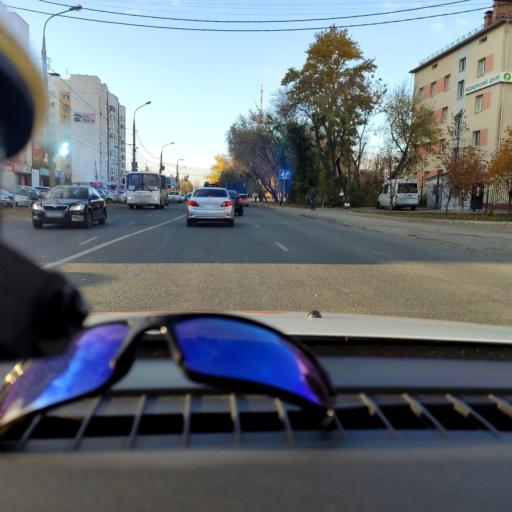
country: RU
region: Samara
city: Samara
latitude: 53.2239
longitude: 50.1997
